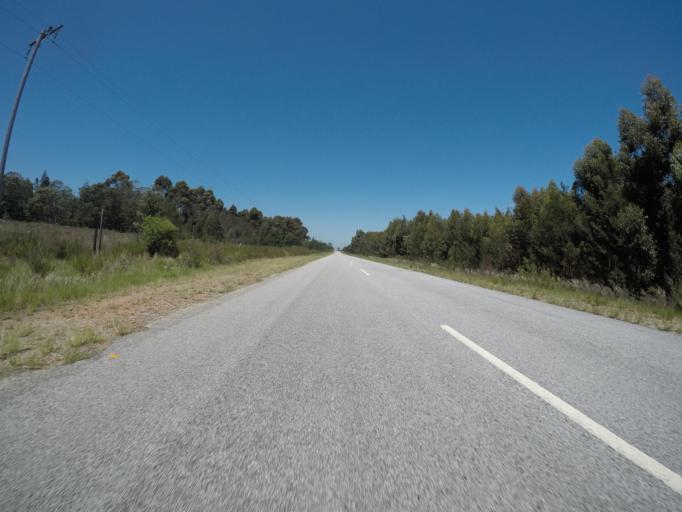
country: ZA
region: Eastern Cape
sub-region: Cacadu District Municipality
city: Kareedouw
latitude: -33.9688
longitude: 24.4559
